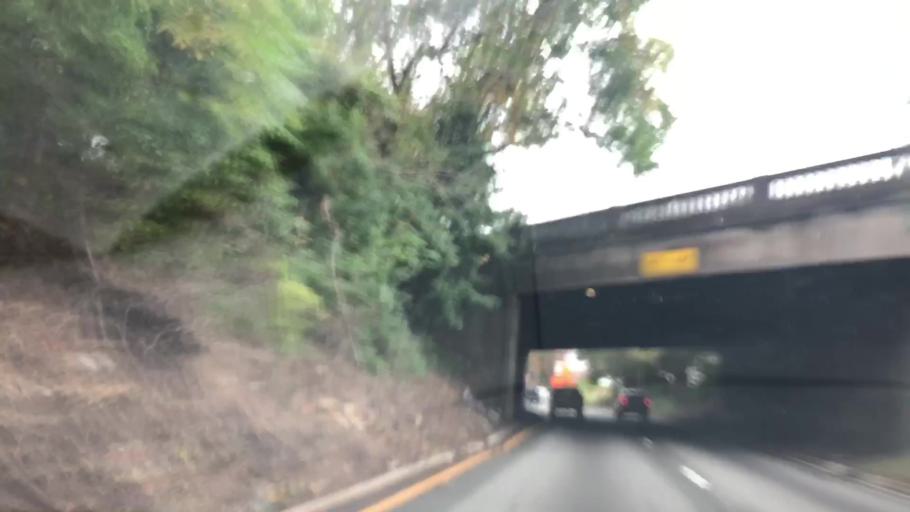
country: US
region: New Jersey
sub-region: Passaic County
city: Woodland Park
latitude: 40.8697
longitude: -74.1863
